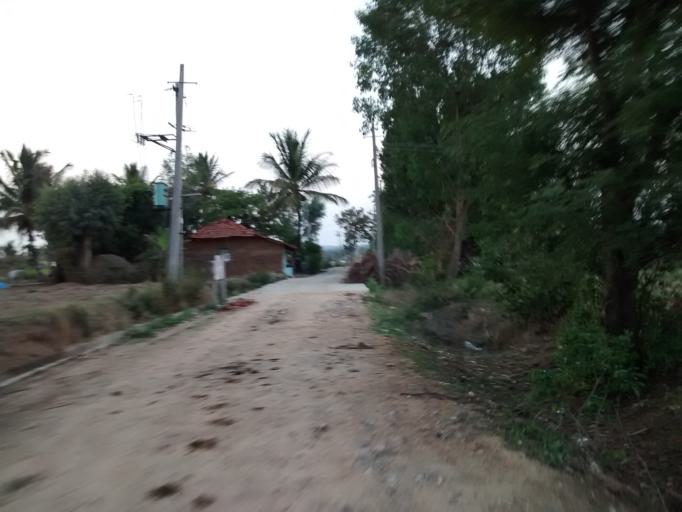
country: IN
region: Karnataka
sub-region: Hassan
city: Hassan
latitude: 12.9413
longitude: 76.1552
